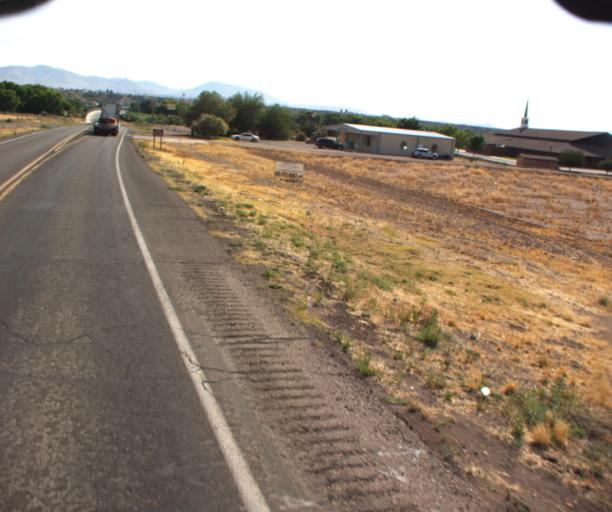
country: US
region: Arizona
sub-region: Greenlee County
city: Clifton
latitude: 32.7268
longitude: -109.0962
